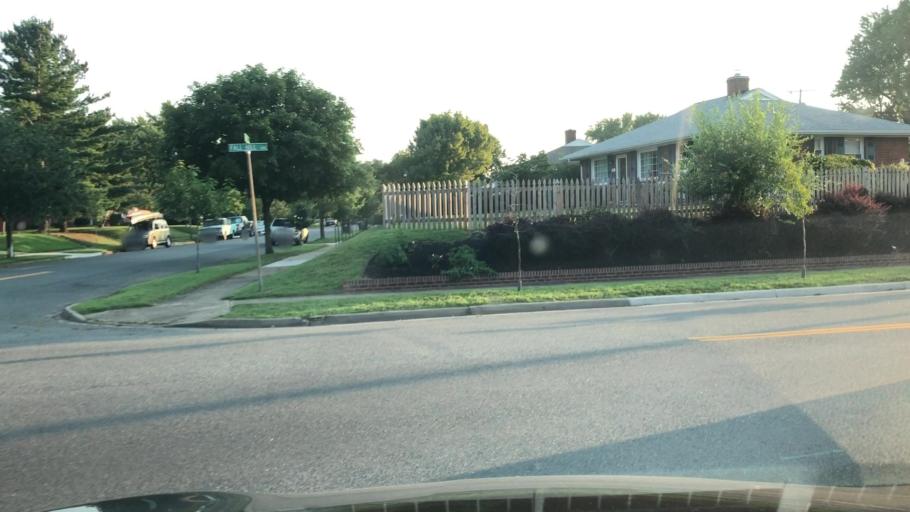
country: US
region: Virginia
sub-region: Stafford County
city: Falmouth
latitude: 38.3157
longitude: -77.4779
